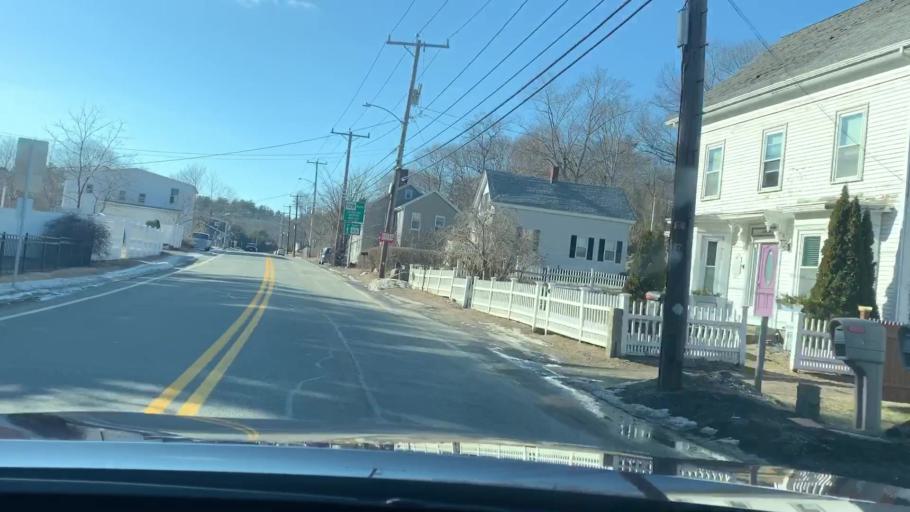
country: US
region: Massachusetts
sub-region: Essex County
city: Gloucester
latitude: 42.6179
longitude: -70.7171
